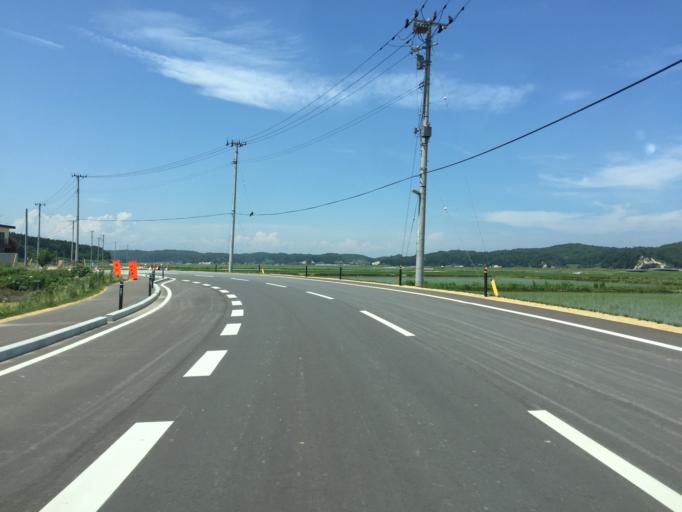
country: JP
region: Fukushima
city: Namie
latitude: 37.7213
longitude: 140.9976
